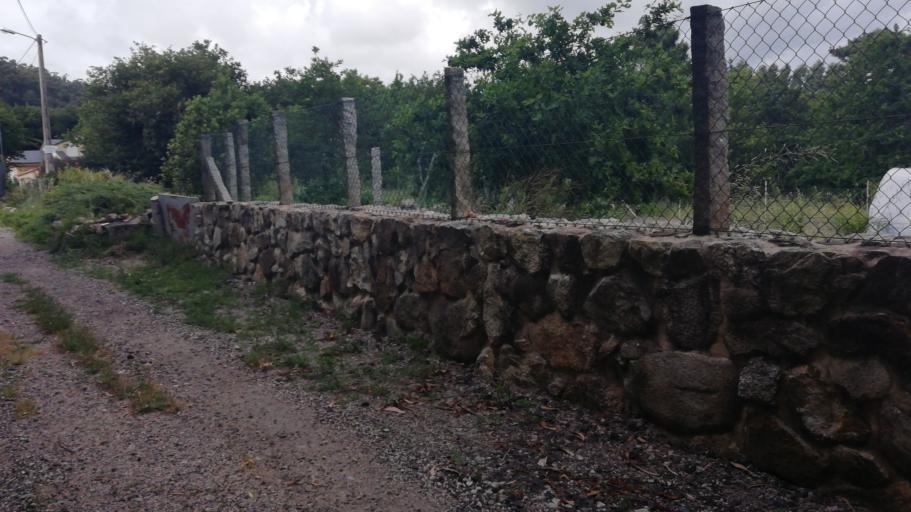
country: ES
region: Galicia
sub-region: Provincia de Pontevedra
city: A Guarda
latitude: 41.8832
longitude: -8.8604
